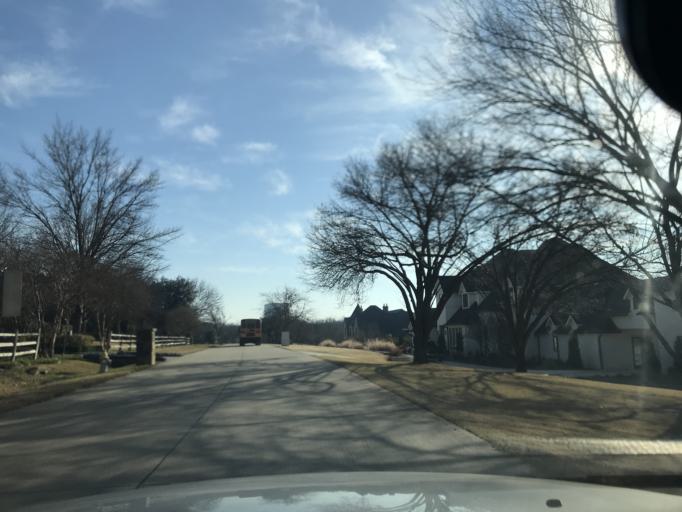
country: US
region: Texas
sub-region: Denton County
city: The Colony
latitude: 33.0973
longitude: -96.8365
